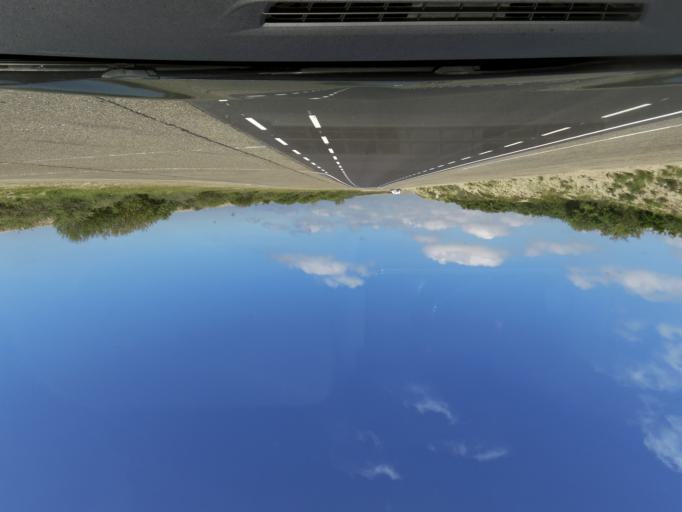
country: NL
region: Zeeland
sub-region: Schouwen-Duiveland
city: Scharendijke
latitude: 51.7628
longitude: 3.8536
